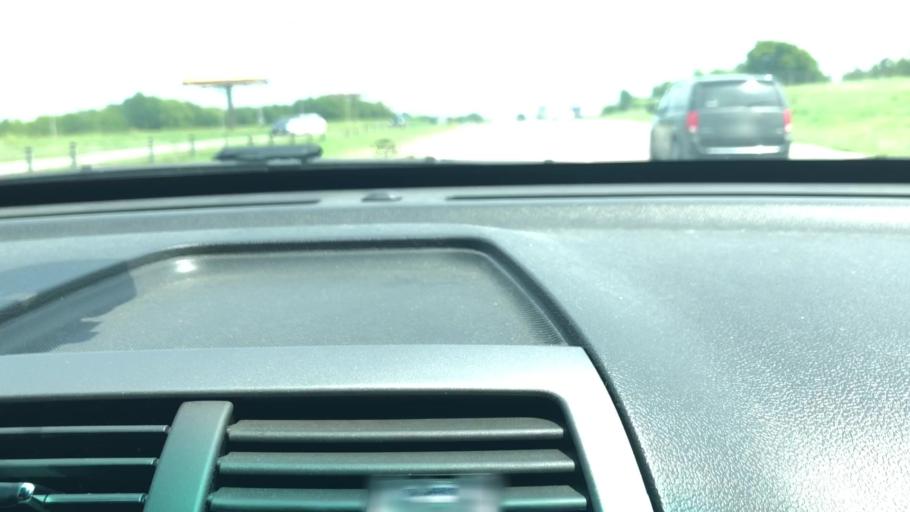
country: US
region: Oklahoma
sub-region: Rogers County
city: Catoosa
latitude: 36.1625
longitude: -95.7876
